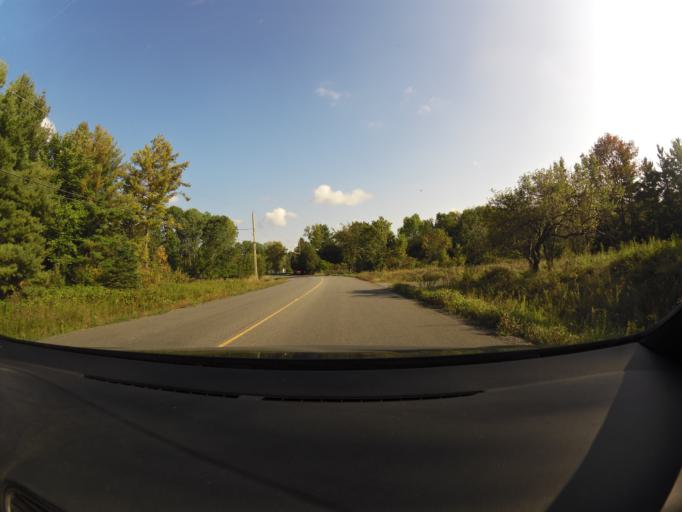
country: CA
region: Ontario
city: Arnprior
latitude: 45.4425
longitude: -76.2608
